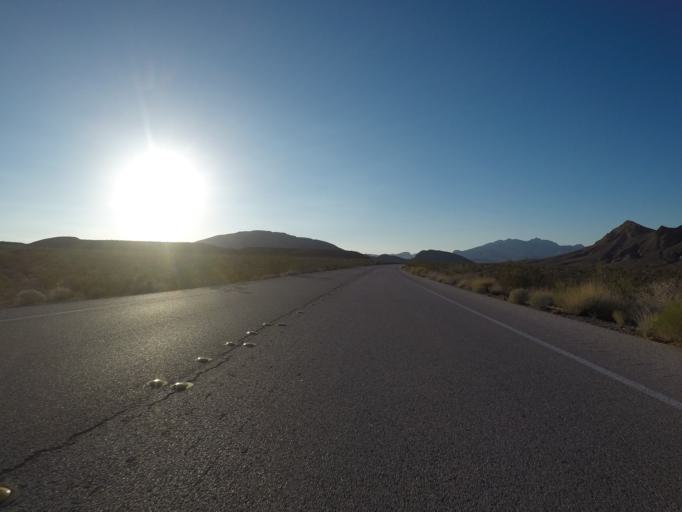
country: US
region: Nevada
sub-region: Clark County
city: Moapa Valley
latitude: 36.2415
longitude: -114.5262
